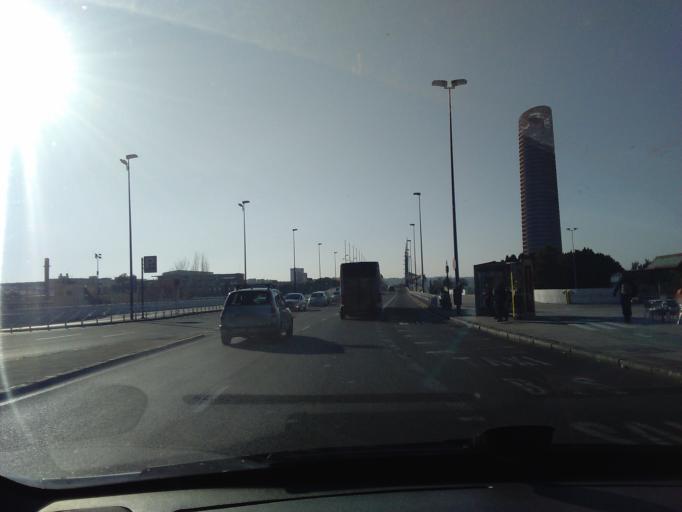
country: ES
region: Andalusia
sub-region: Provincia de Sevilla
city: Sevilla
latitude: 37.3908
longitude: -6.0036
